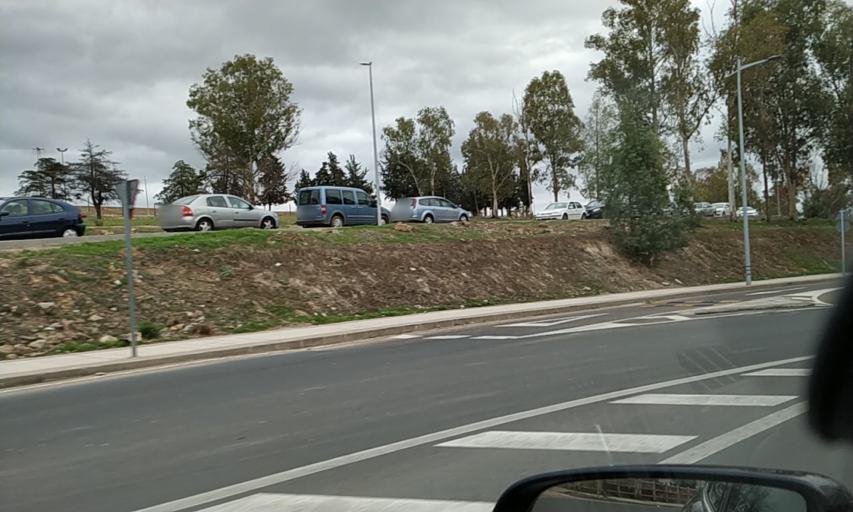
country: ES
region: Extremadura
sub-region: Provincia de Badajoz
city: Badajoz
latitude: 38.8892
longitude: -6.9757
